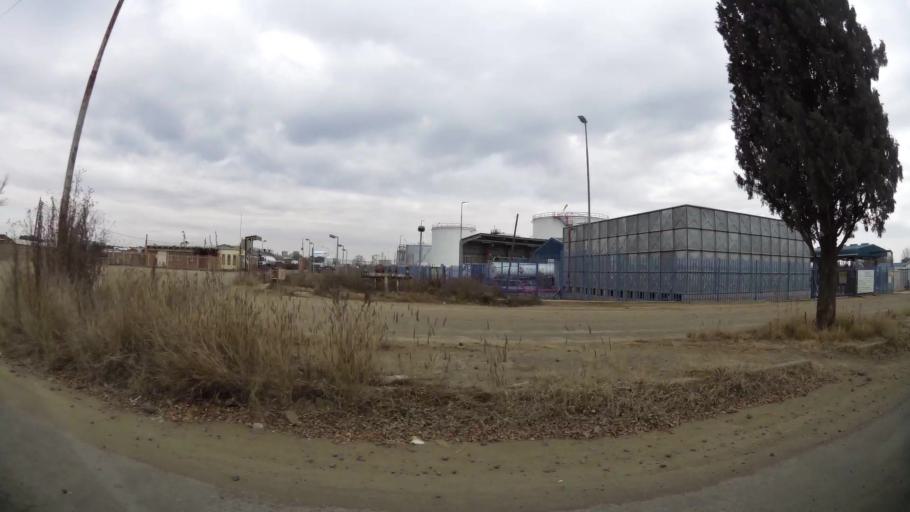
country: ZA
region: Orange Free State
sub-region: Fezile Dabi District Municipality
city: Kroonstad
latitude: -27.6743
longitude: 27.2308
